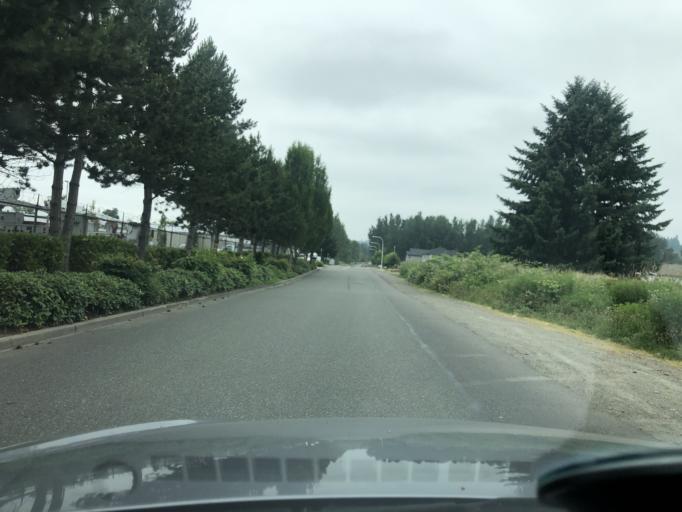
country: US
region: Washington
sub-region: King County
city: Auburn
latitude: 47.3429
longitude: -122.2194
